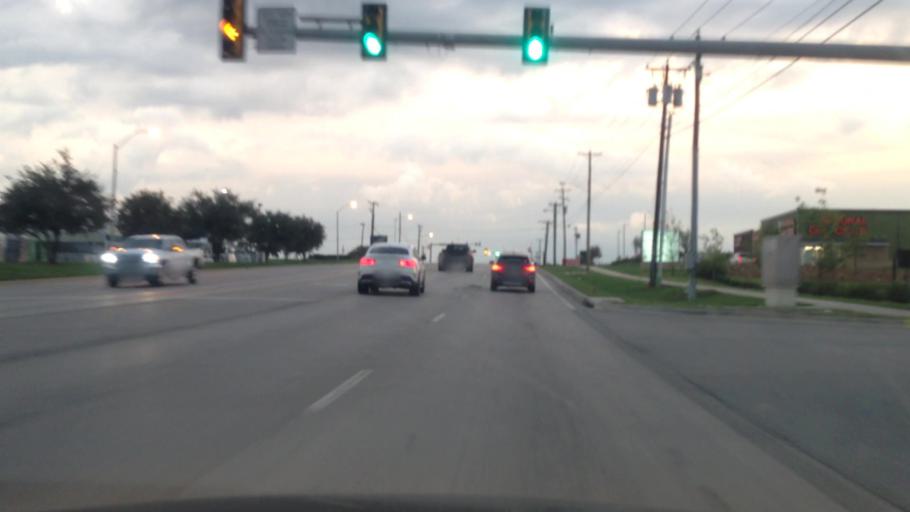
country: US
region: Texas
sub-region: Tarrant County
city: Hurst
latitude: 32.8575
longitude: -97.1839
